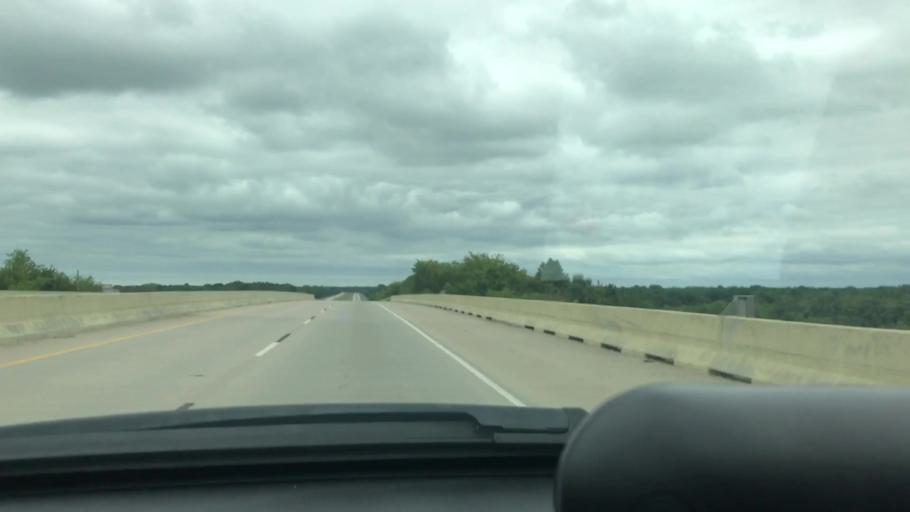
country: US
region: Oklahoma
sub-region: Wagoner County
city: Wagoner
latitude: 35.8858
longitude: -95.4026
